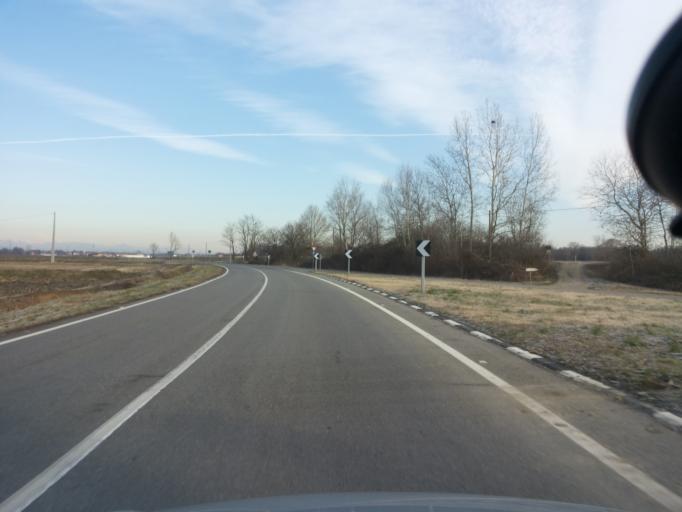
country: IT
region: Piedmont
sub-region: Provincia di Vercelli
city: Albano Vercellese
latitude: 45.4364
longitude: 8.3821
